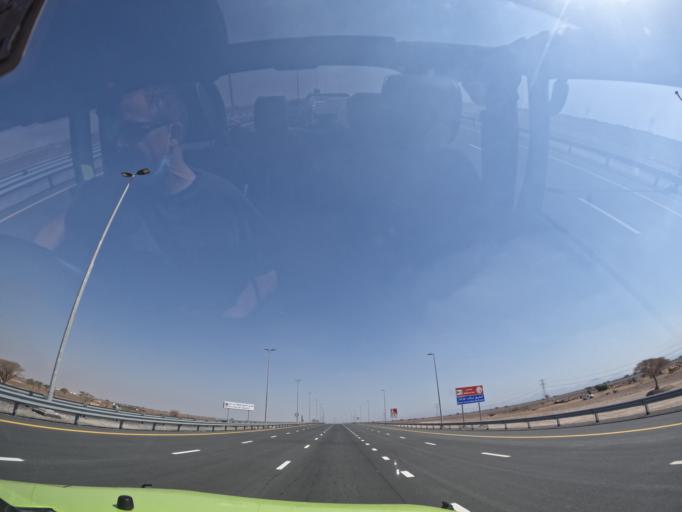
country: AE
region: Ash Shariqah
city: Adh Dhayd
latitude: 24.9344
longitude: 55.8201
